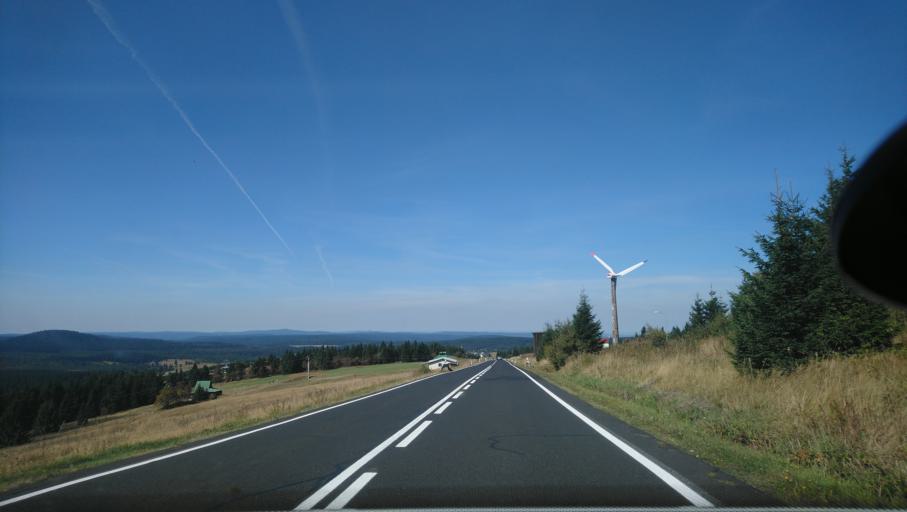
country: DE
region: Saxony
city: Kurort Oberwiesenthal
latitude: 50.4025
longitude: 12.9453
